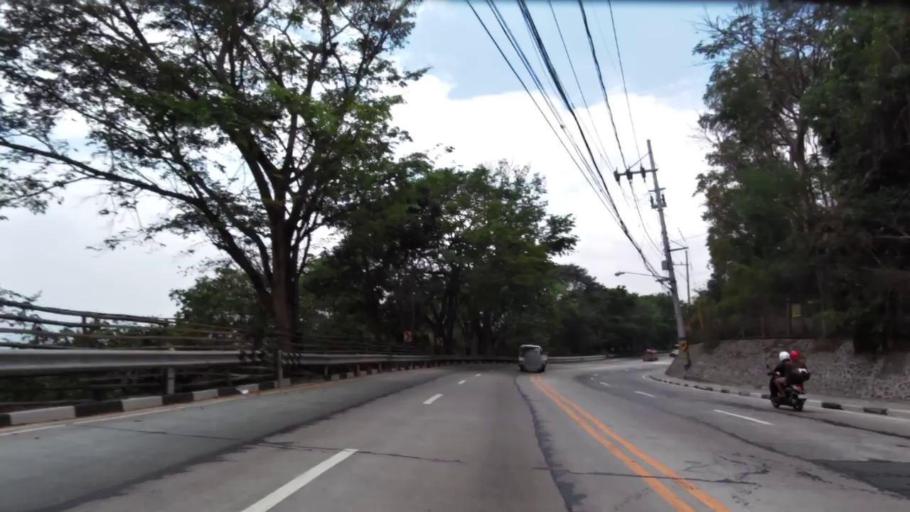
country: PH
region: Calabarzon
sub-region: Province of Rizal
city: Antipolo
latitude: 14.6138
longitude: 121.1521
